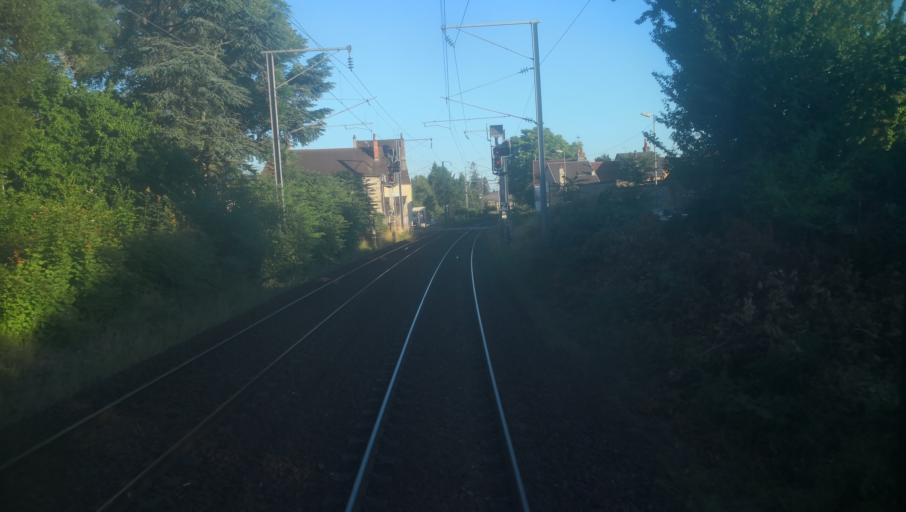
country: FR
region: Auvergne
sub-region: Departement de l'Allier
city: Moulins
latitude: 46.5689
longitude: 3.3410
